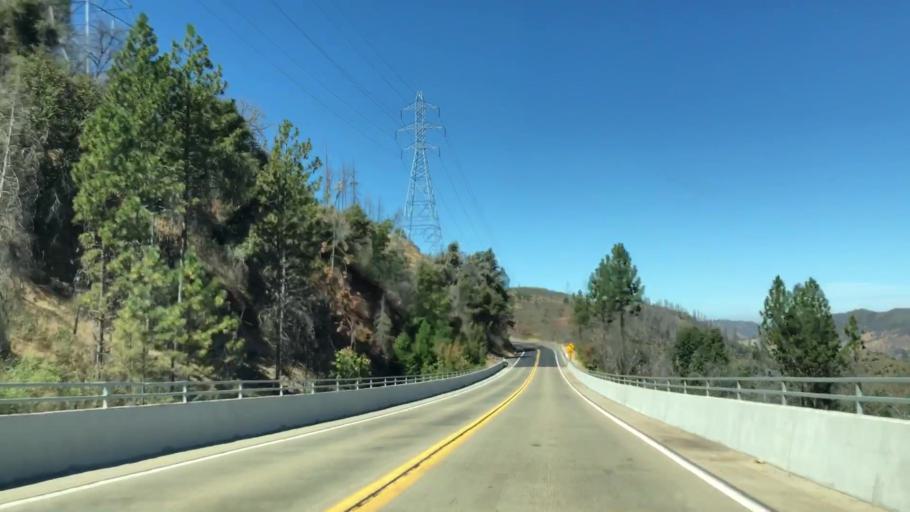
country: US
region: California
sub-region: Tuolumne County
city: Tuolumne City
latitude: 37.8214
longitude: -120.0352
